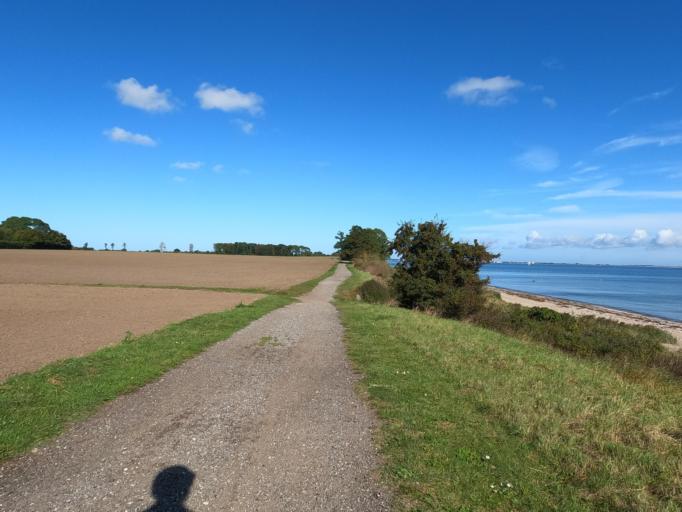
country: DE
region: Schleswig-Holstein
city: Neukirchen
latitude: 54.3118
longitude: 11.0743
